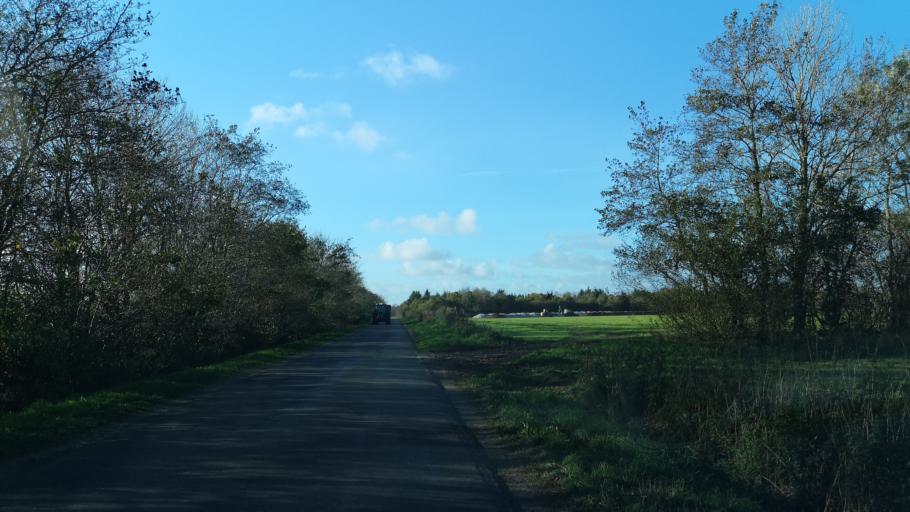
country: DK
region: Central Jutland
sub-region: Ringkobing-Skjern Kommune
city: Tarm
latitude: 55.8259
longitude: 8.3979
